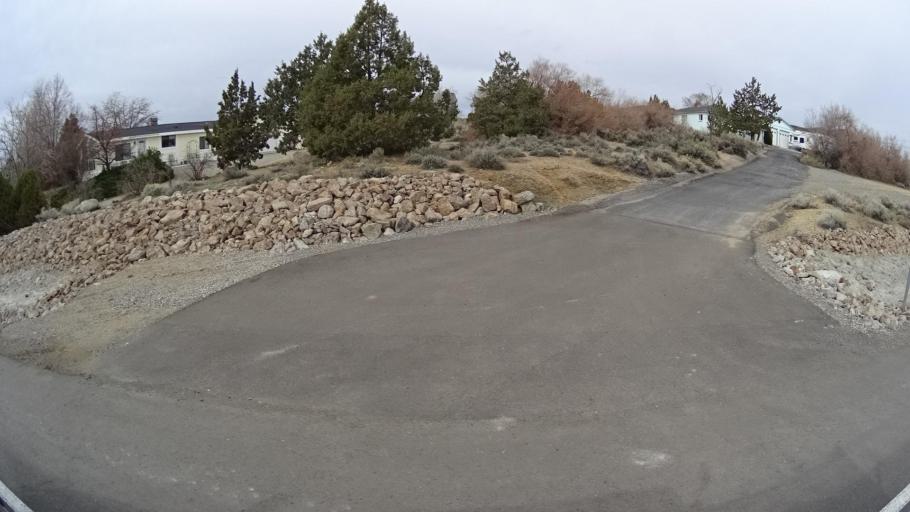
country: US
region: Nevada
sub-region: Washoe County
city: Sun Valley
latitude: 39.6065
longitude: -119.7808
